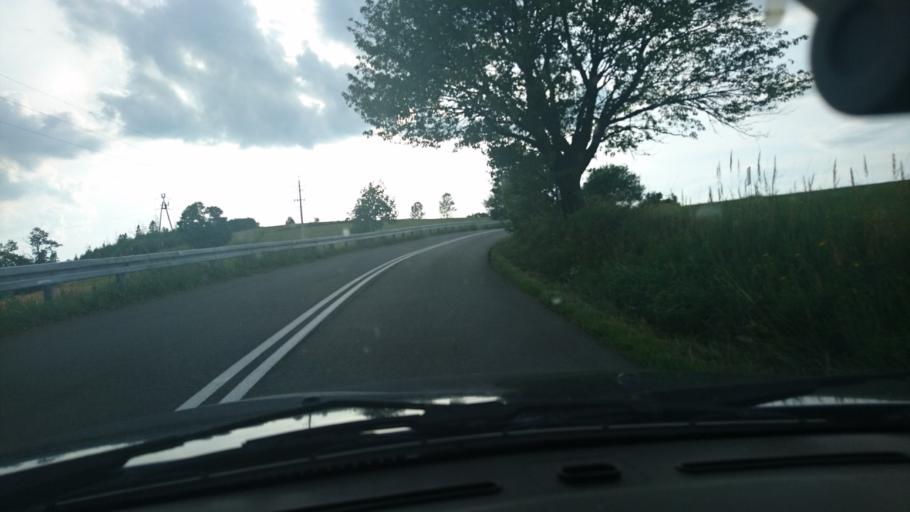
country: PL
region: Silesian Voivodeship
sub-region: Powiat zywiecki
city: Laliki
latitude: 49.5468
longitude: 18.9914
